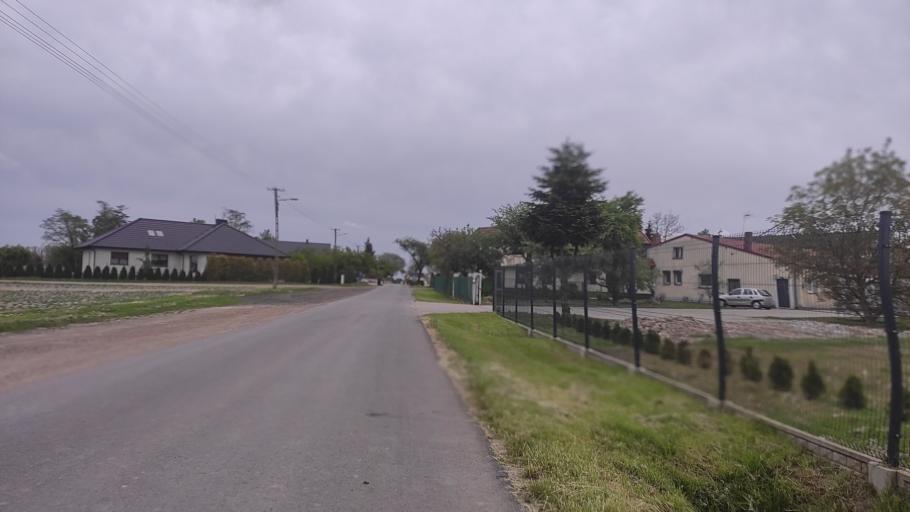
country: PL
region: Greater Poland Voivodeship
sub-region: Powiat poznanski
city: Swarzedz
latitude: 52.4102
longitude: 17.1306
